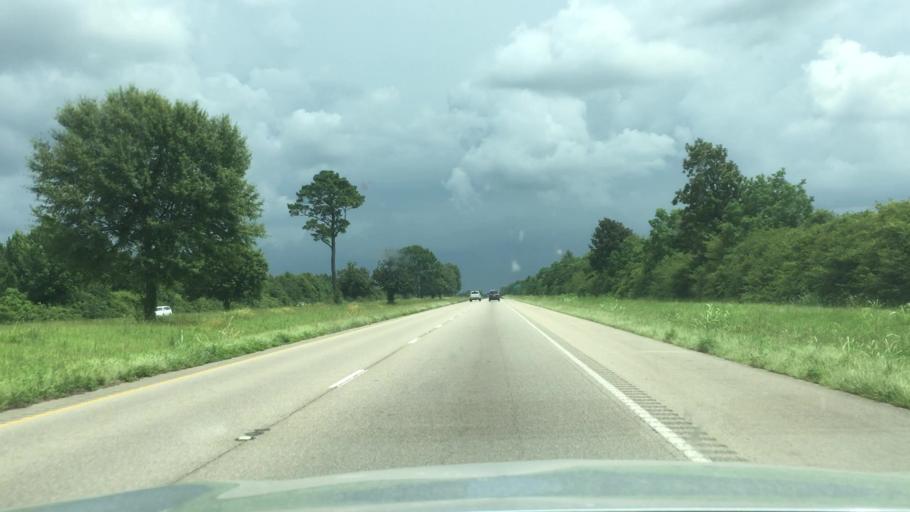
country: US
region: Mississippi
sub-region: Pearl River County
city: Carriere
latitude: 30.5812
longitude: -89.6287
